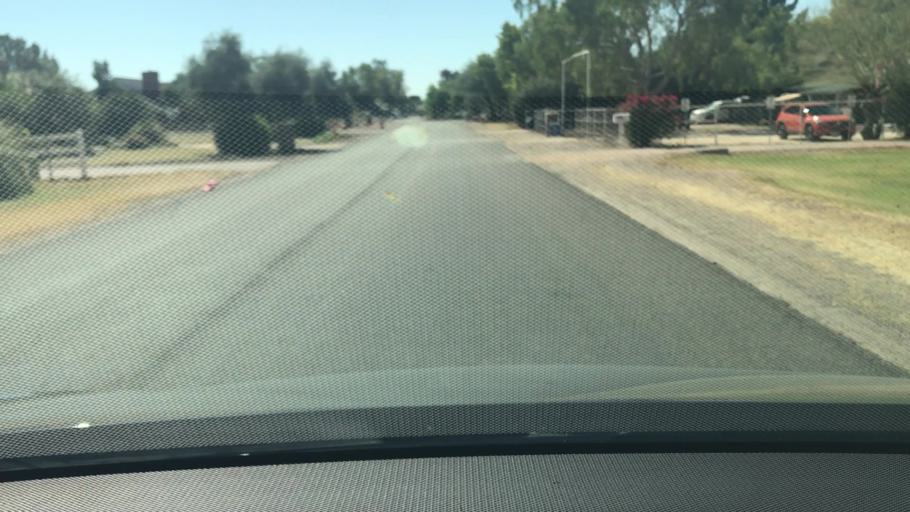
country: US
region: Arizona
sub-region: Maricopa County
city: Gilbert
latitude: 33.3183
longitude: -111.8006
